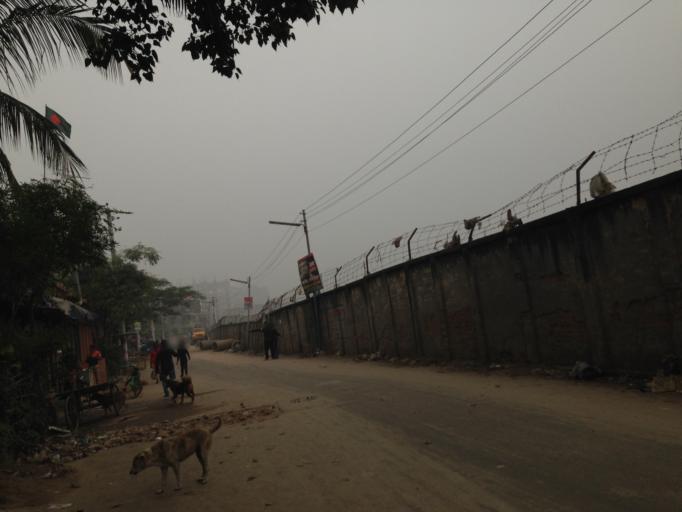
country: BD
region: Dhaka
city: Azimpur
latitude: 23.7960
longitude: 90.3430
